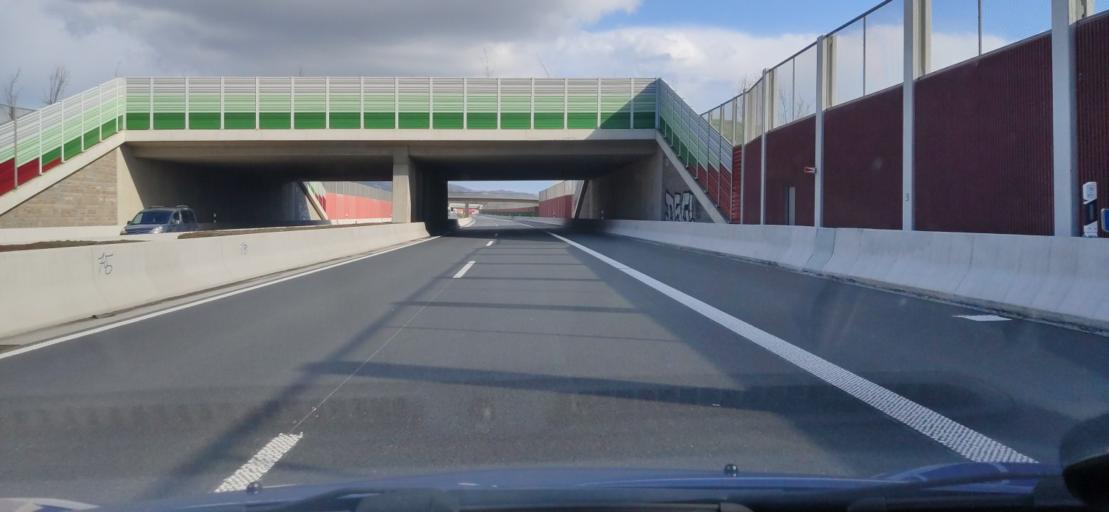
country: DE
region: North Rhine-Westphalia
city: Borgholzhausen
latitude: 52.0676
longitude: 8.2743
